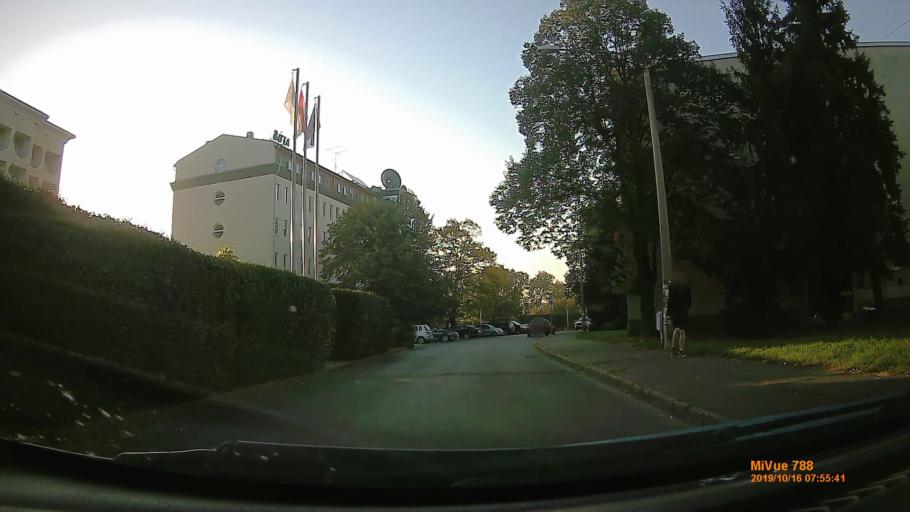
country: HU
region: Heves
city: Eger
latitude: 47.8965
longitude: 20.3765
